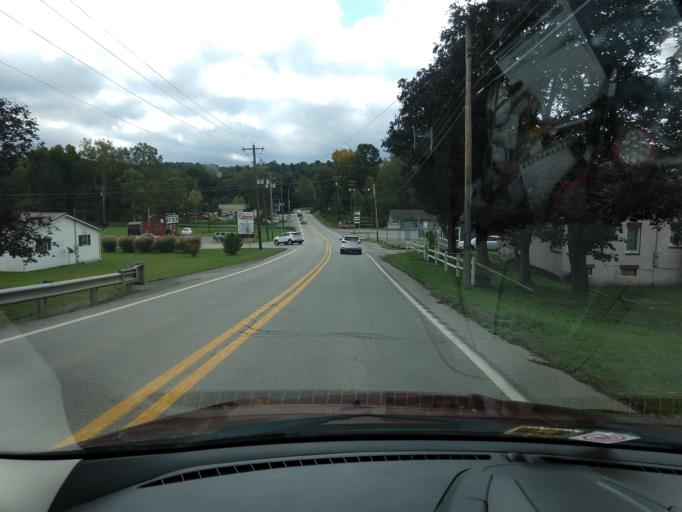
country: US
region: West Virginia
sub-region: Barbour County
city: Belington
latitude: 39.0136
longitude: -79.9389
